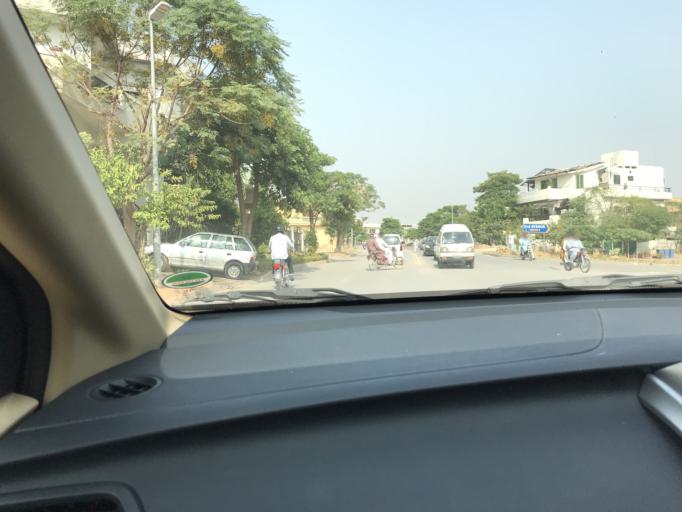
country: PK
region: Punjab
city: Rawalpindi
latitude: 33.5269
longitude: 73.1049
